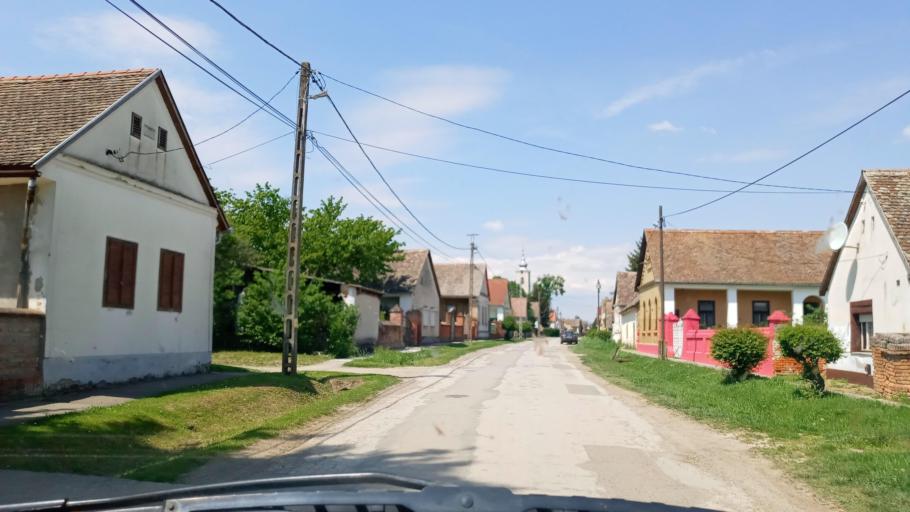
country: HU
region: Baranya
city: Villany
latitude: 45.8724
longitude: 18.5107
